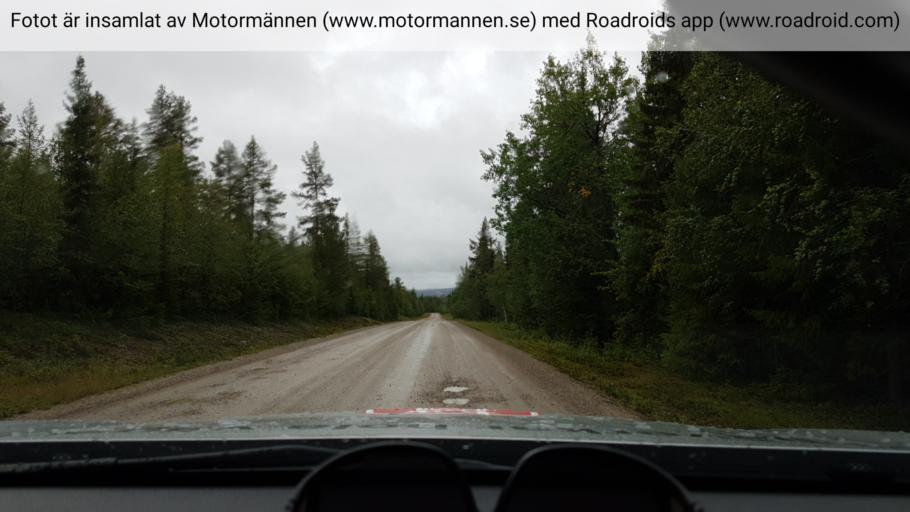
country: SE
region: Vaesterbotten
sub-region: Asele Kommun
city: Insjon
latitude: 64.7489
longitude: 17.6527
